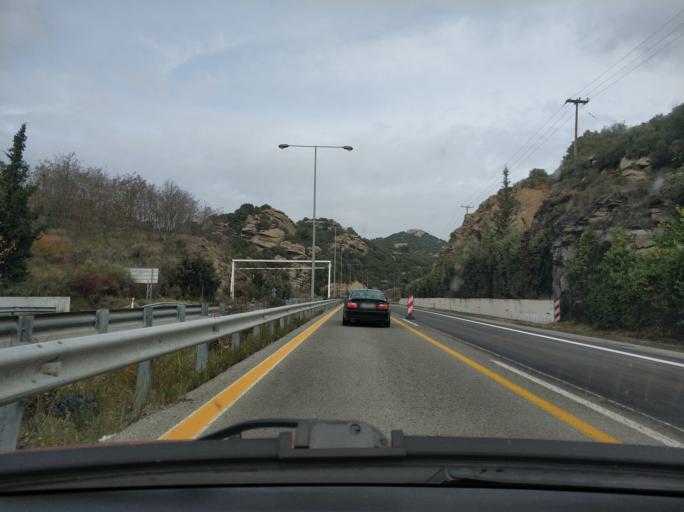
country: GR
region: East Macedonia and Thrace
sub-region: Nomos Kavalas
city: Palaio Tsifliki
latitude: 40.9121
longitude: 24.3589
